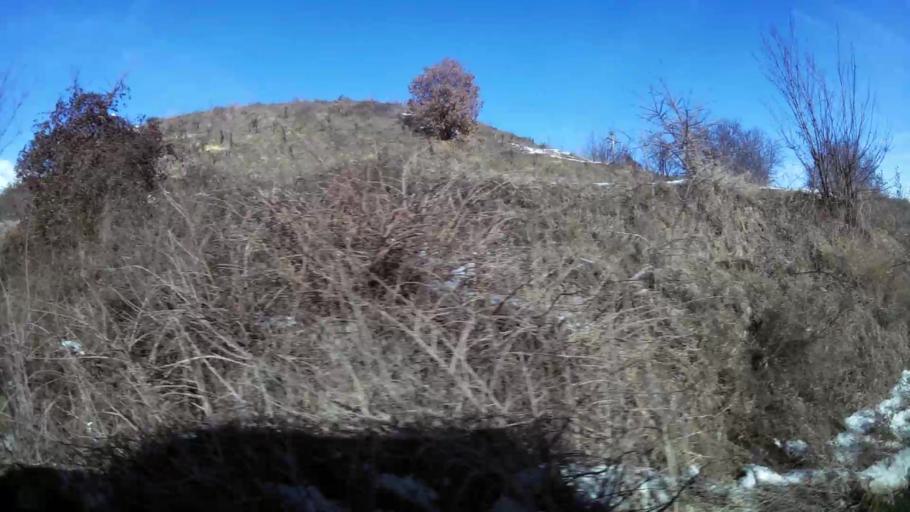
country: MK
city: Ljubin
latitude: 41.9855
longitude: 21.3054
